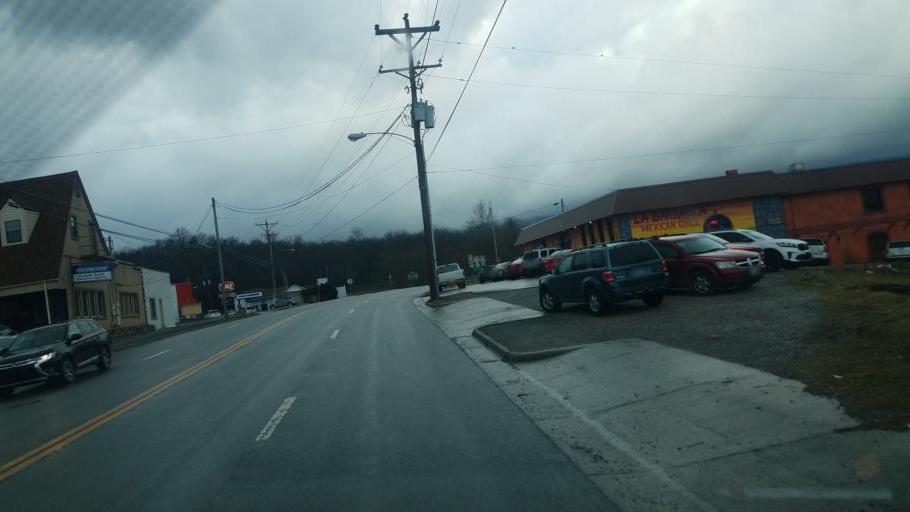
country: US
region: Virginia
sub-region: Giles County
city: Pearisburg
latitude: 37.3301
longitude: -80.7376
